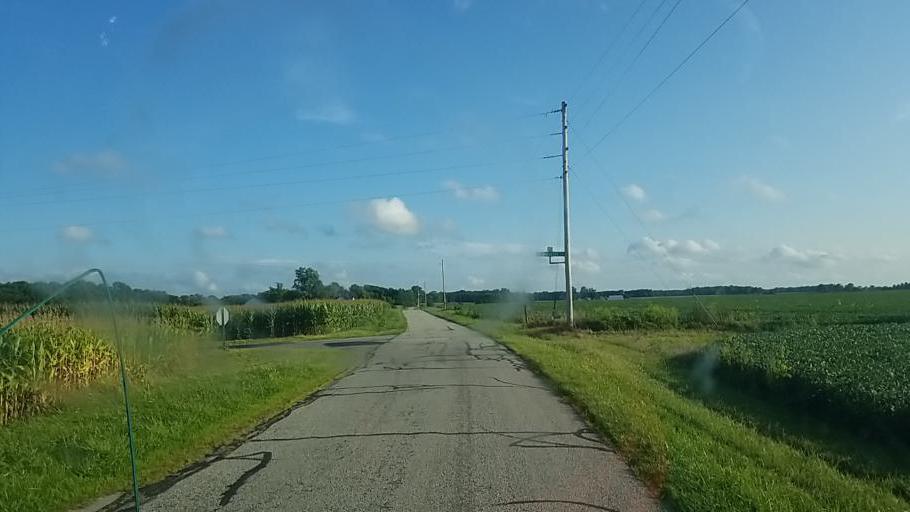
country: US
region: Ohio
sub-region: Crawford County
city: Bucyrus
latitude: 40.7331
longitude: -82.9365
